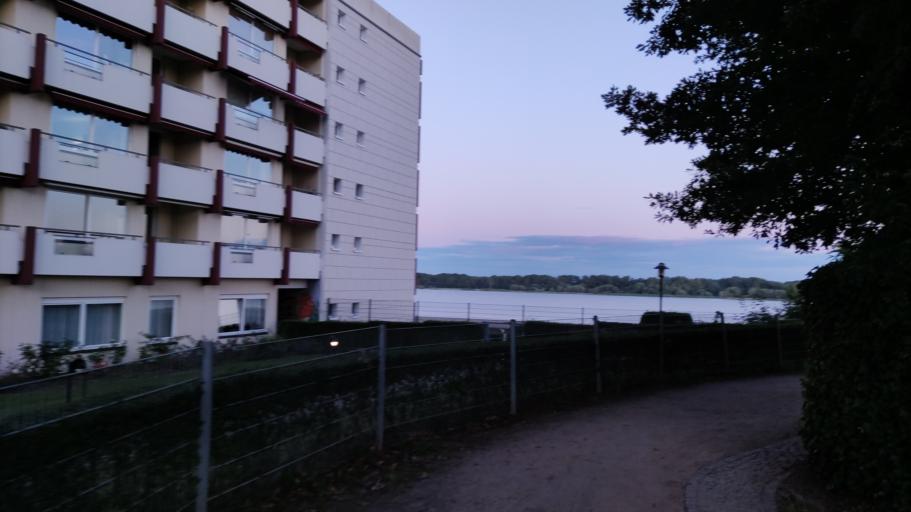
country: DE
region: Schleswig-Holstein
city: Wedel
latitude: 53.5679
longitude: 9.7142
